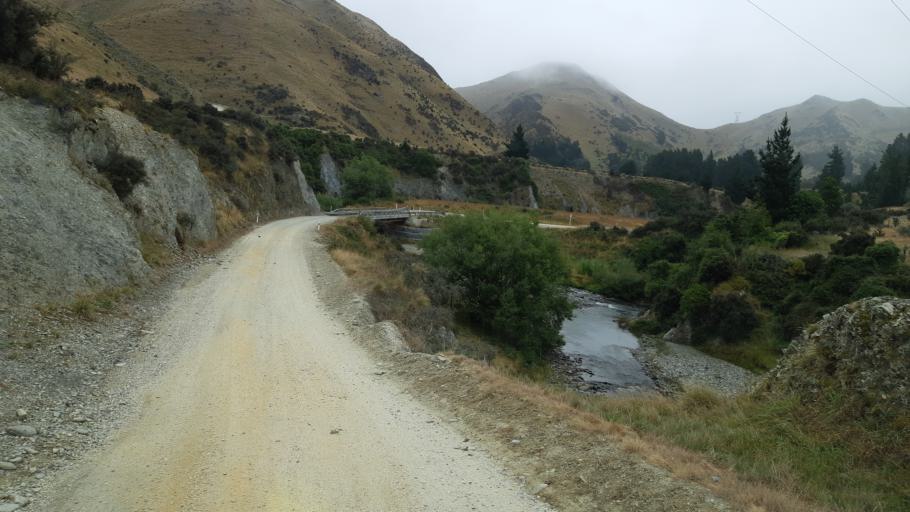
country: NZ
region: Otago
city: Oamaru
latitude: -44.9559
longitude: 170.4822
